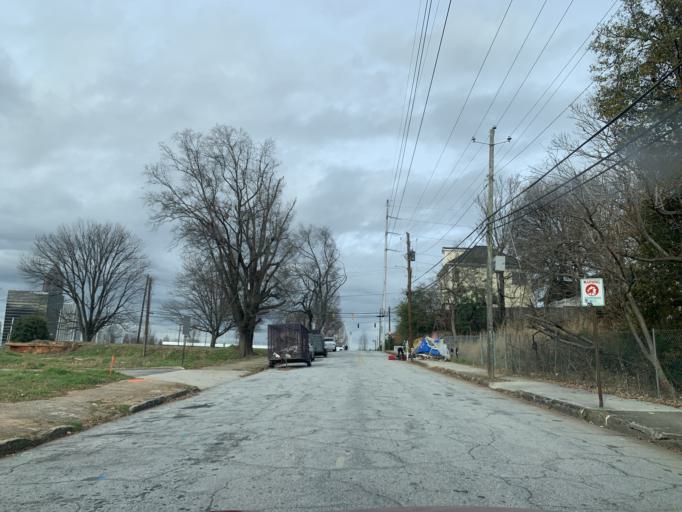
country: US
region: Georgia
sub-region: Fulton County
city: Atlanta
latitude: 33.7569
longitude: -84.3765
